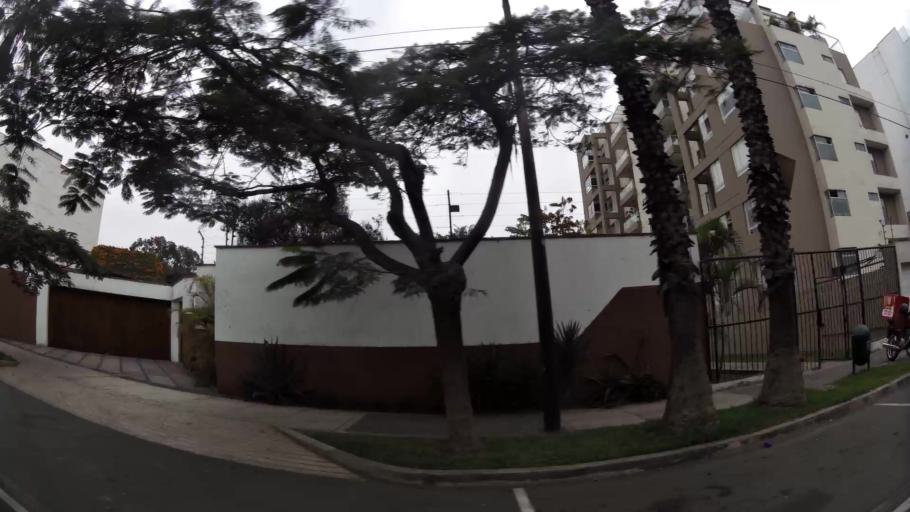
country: PE
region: Lima
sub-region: Lima
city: San Luis
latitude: -12.1016
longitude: -77.0140
